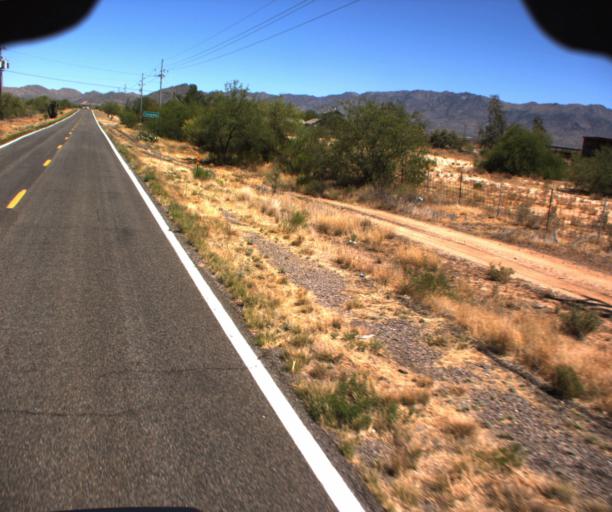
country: US
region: Arizona
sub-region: Yavapai County
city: Congress
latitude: 34.1425
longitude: -112.8417
